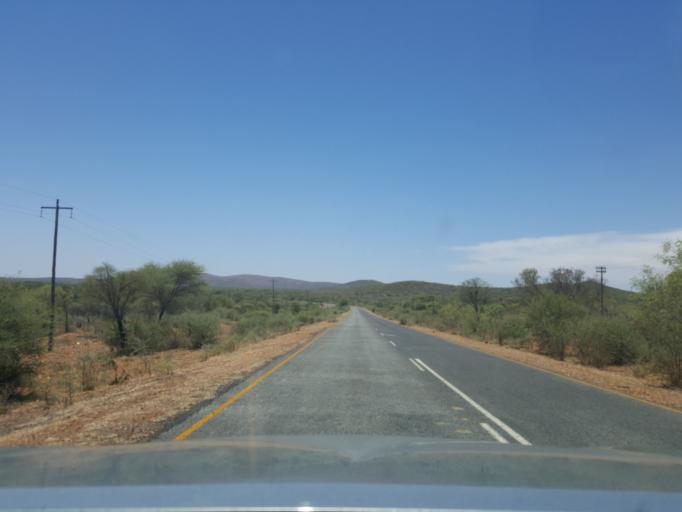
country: BW
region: South East
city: Ramotswa
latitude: -24.8890
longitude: 25.8882
